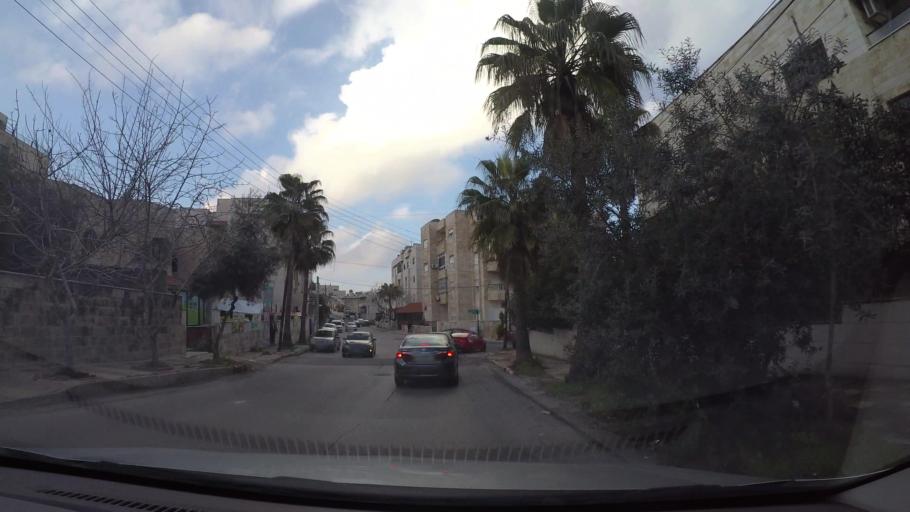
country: JO
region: Amman
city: Al Jubayhah
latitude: 31.9852
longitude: 35.8607
